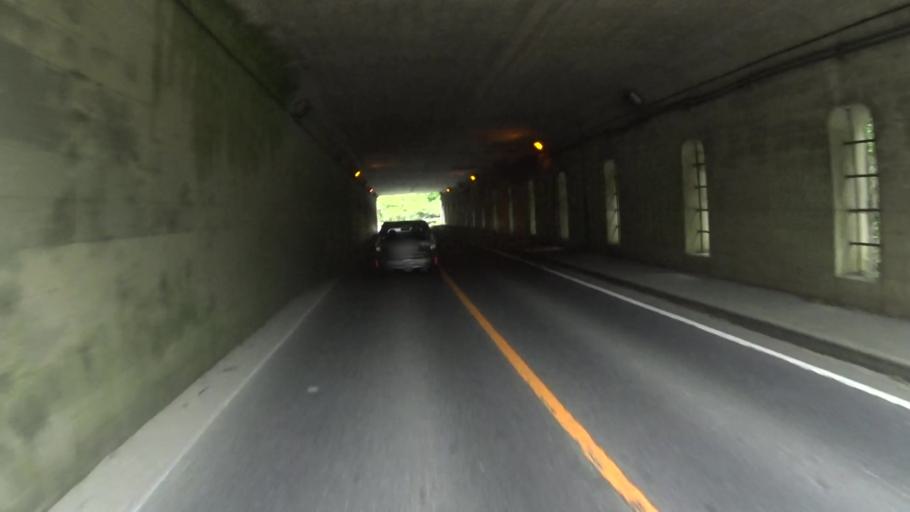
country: JP
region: Kyoto
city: Uji
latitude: 34.8622
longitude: 135.8403
